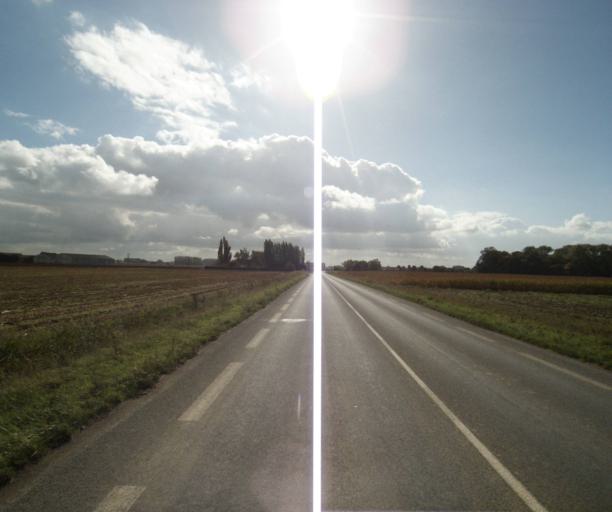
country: FR
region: Nord-Pas-de-Calais
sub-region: Departement du Nord
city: Frelinghien
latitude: 50.7185
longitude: 2.9394
